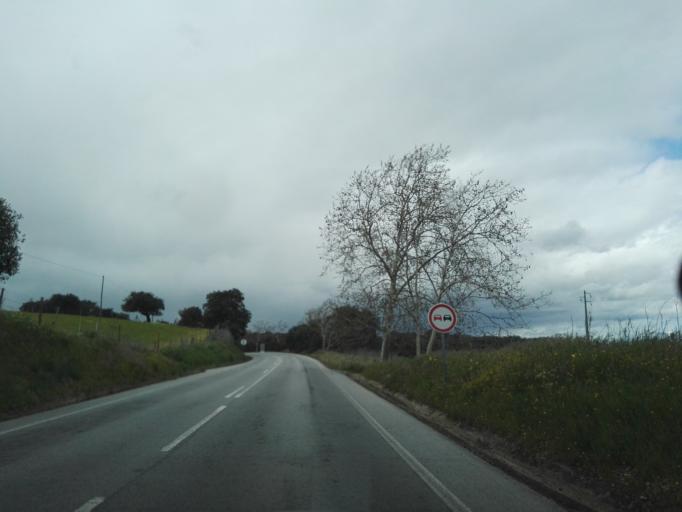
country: PT
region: Portalegre
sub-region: Elvas
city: Elvas
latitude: 38.9753
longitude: -7.2309
